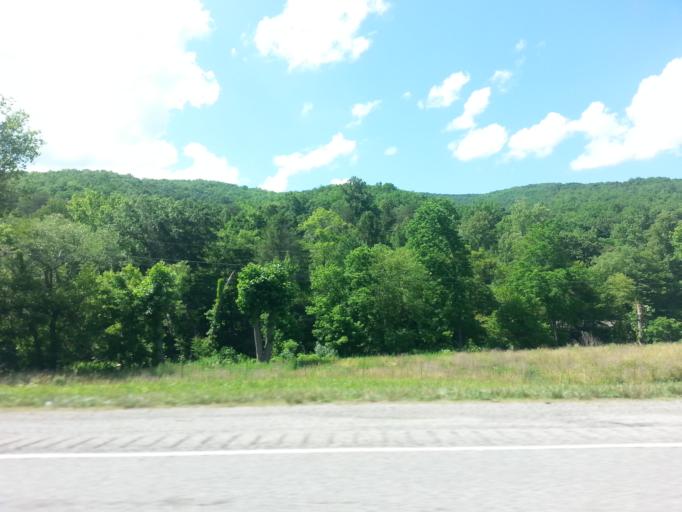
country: US
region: Kentucky
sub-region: Harlan County
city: Harlan
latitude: 36.9170
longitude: -83.1852
